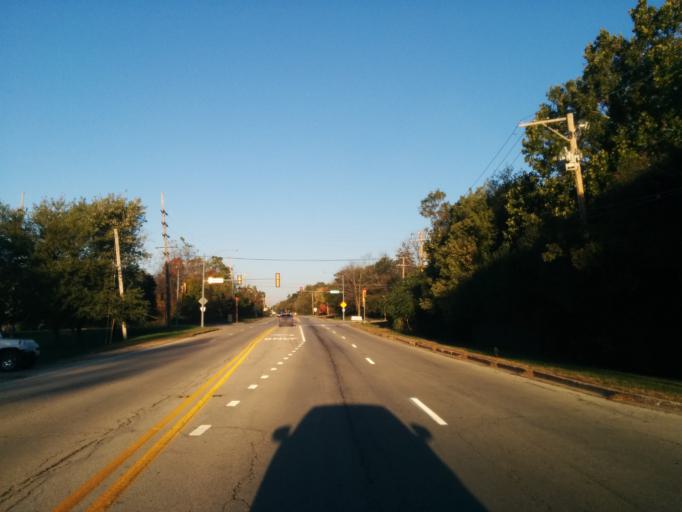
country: US
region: Illinois
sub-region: DuPage County
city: Glendale Heights
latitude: 41.8944
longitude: -88.0809
